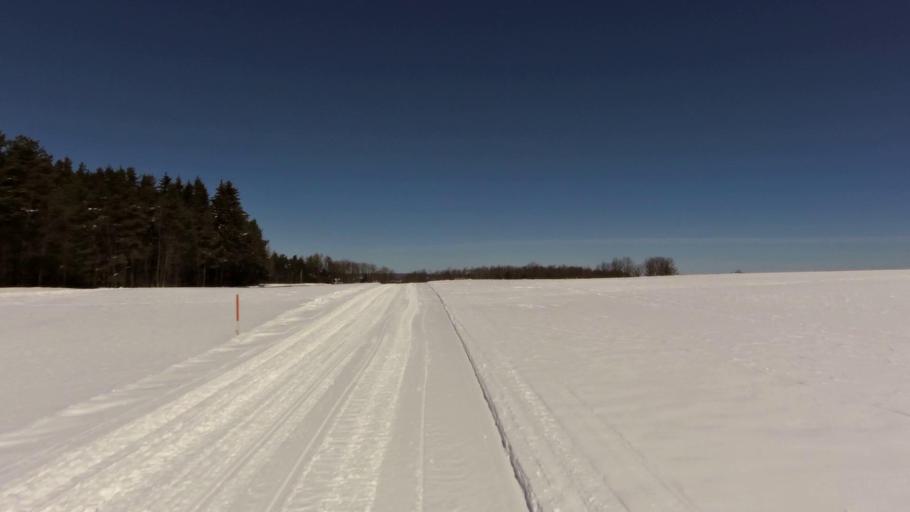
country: US
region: New York
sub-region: Allegany County
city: Houghton
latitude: 42.3558
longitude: -78.2608
